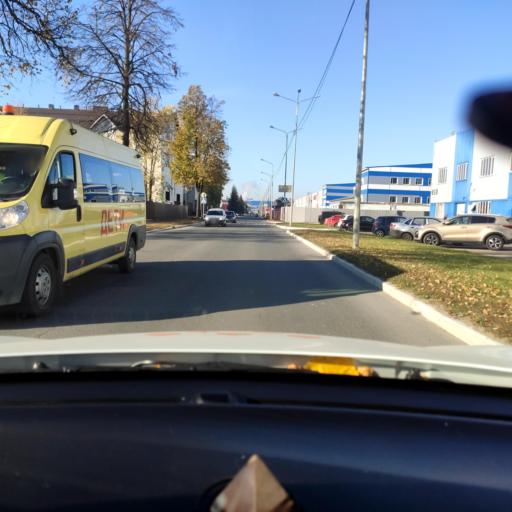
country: RU
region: Tatarstan
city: Staroye Arakchino
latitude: 55.8341
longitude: 49.0482
